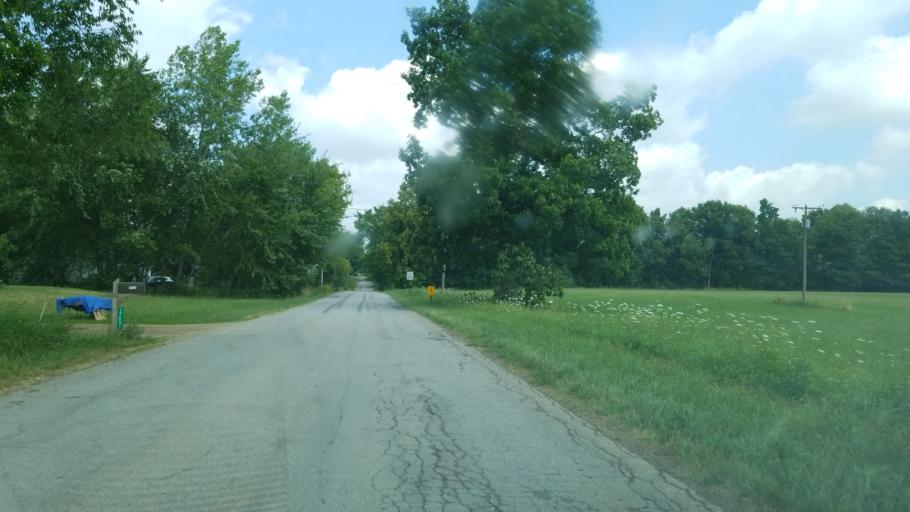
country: US
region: Michigan
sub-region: Kent County
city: Cedar Springs
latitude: 43.2878
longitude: -85.5115
